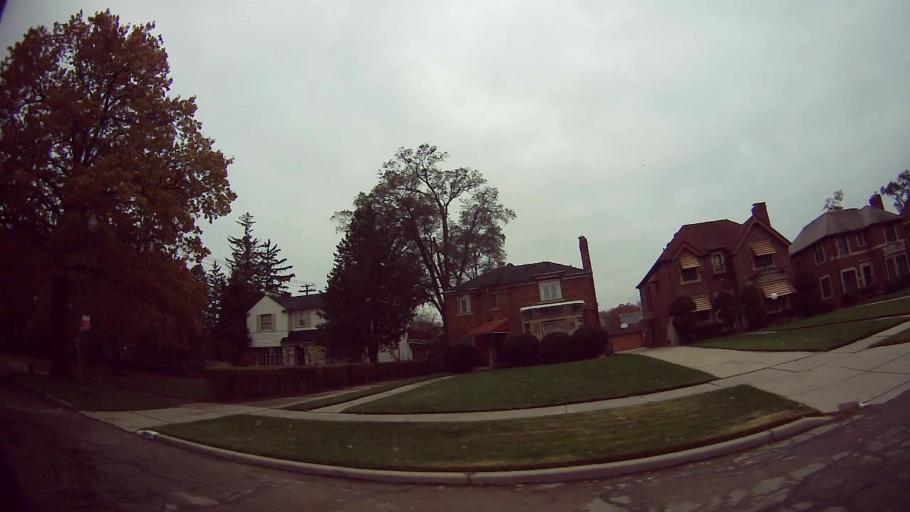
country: US
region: Michigan
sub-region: Oakland County
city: Oak Park
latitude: 42.4332
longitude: -83.1756
